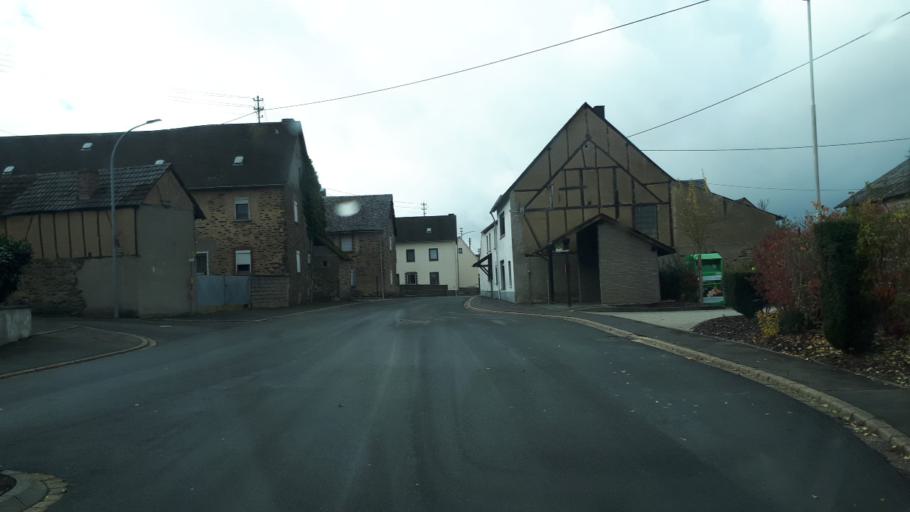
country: DE
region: Rheinland-Pfalz
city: Wirfus
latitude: 50.1995
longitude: 7.2056
